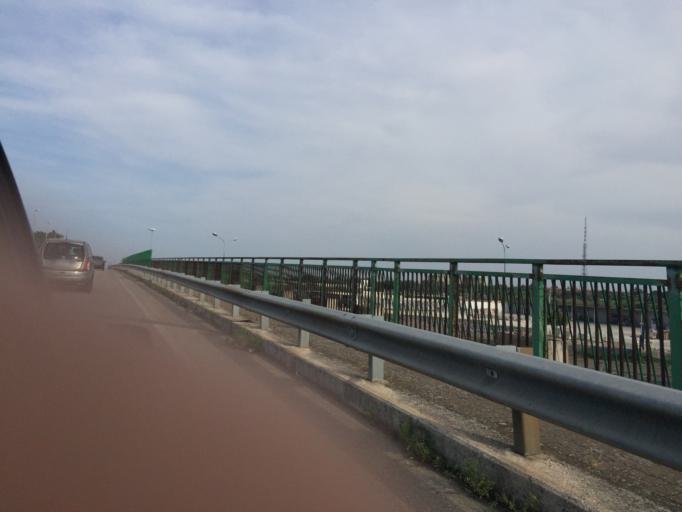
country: IT
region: Apulia
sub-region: Provincia di Bari
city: Triggiano
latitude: 41.1006
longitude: 16.9138
